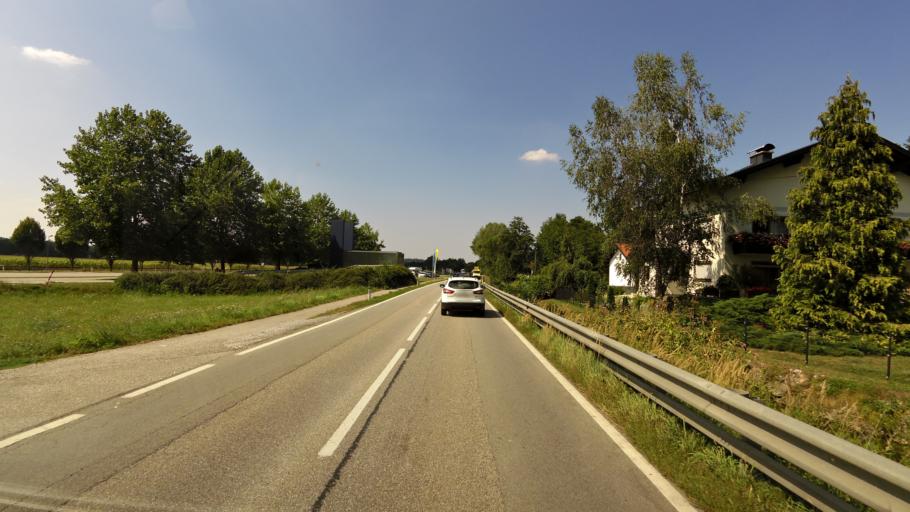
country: AT
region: Upper Austria
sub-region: Politischer Bezirk Braunau am Inn
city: Altheim
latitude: 48.1392
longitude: 13.1371
